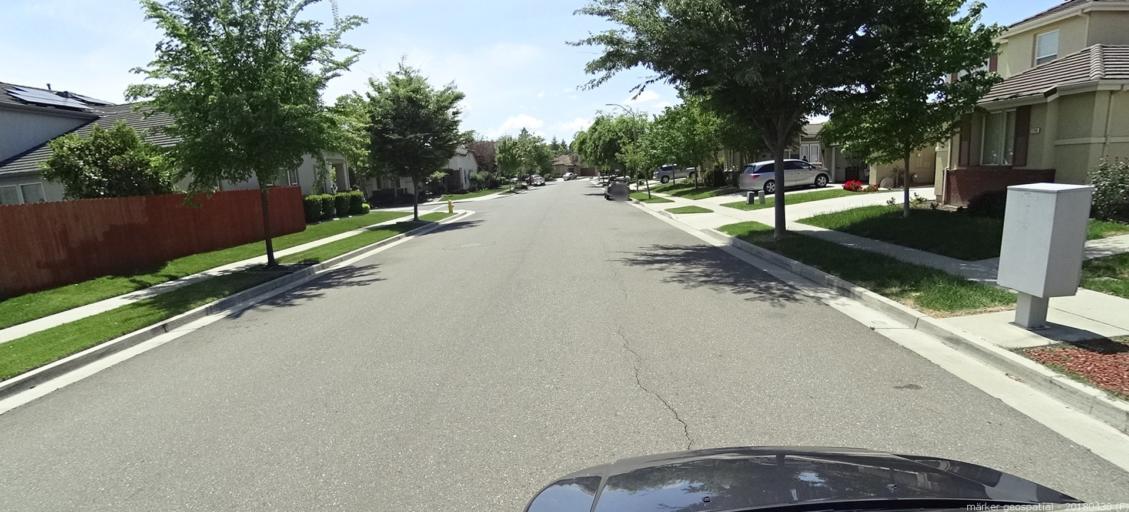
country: US
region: California
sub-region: Yolo County
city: West Sacramento
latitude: 38.5479
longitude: -121.5304
